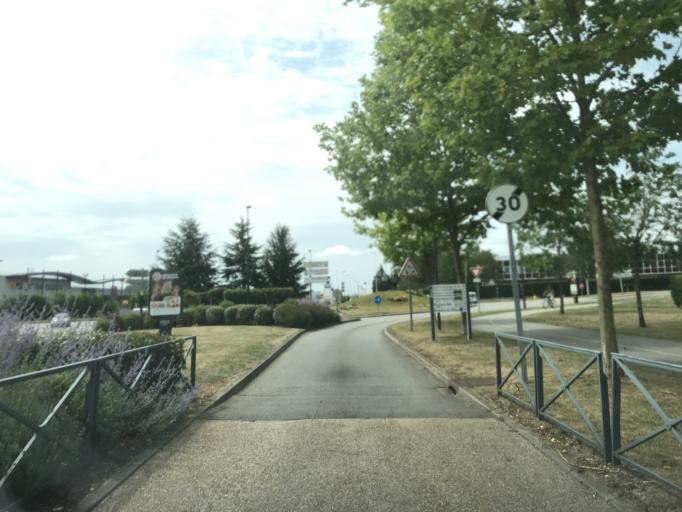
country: FR
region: Ile-de-France
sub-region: Departement des Yvelines
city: Maurepas
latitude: 48.7605
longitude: 1.9349
